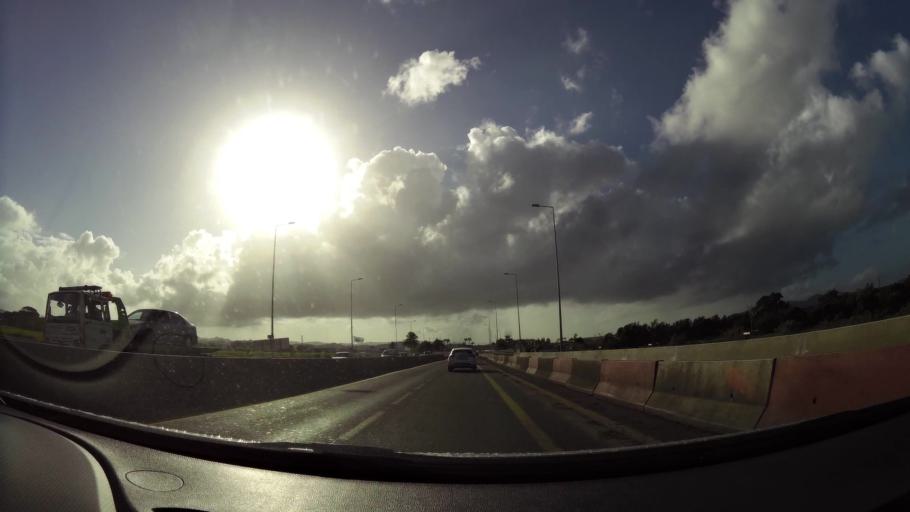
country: MQ
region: Martinique
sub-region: Martinique
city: Le Lamentin
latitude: 14.6024
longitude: -61.0015
